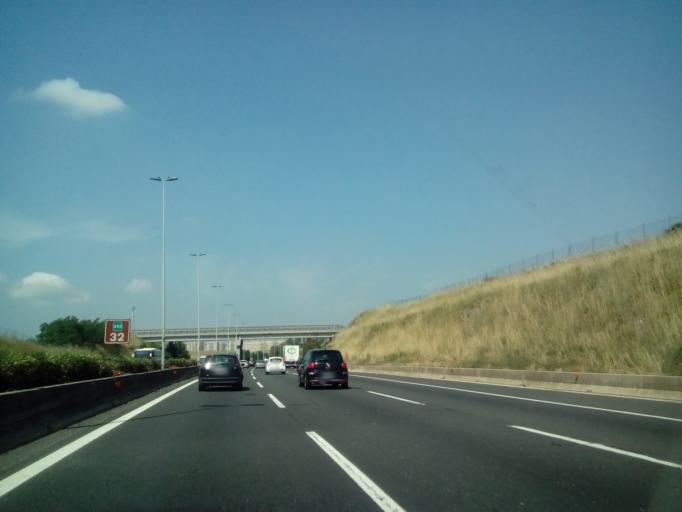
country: IT
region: Latium
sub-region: Citta metropolitana di Roma Capitale
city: Selcetta
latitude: 41.7944
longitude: 12.5131
